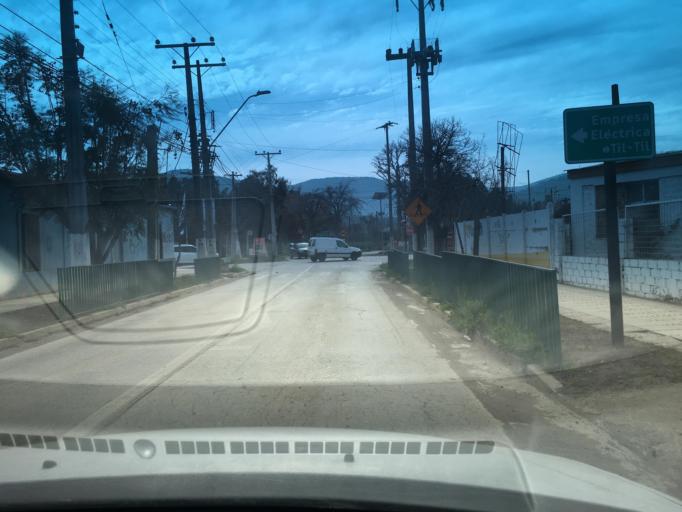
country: CL
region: Santiago Metropolitan
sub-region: Provincia de Chacabuco
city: Lampa
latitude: -33.0832
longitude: -70.9284
